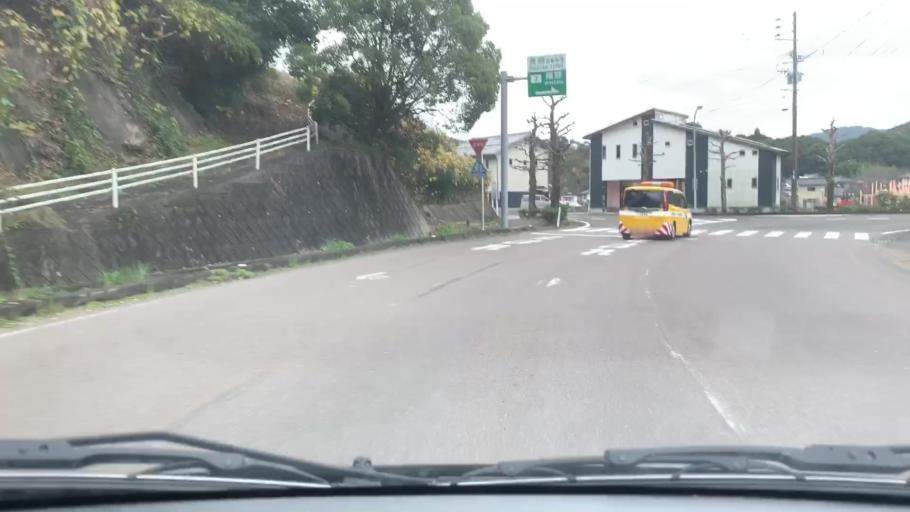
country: JP
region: Saga Prefecture
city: Ureshinomachi-shimojuku
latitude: 33.1084
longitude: 129.9764
